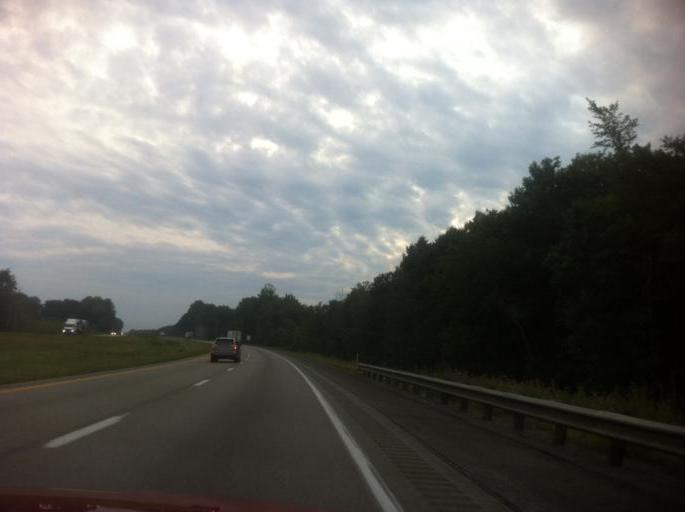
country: US
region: Pennsylvania
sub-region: Mercer County
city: Grove City
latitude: 41.2030
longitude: -79.9853
